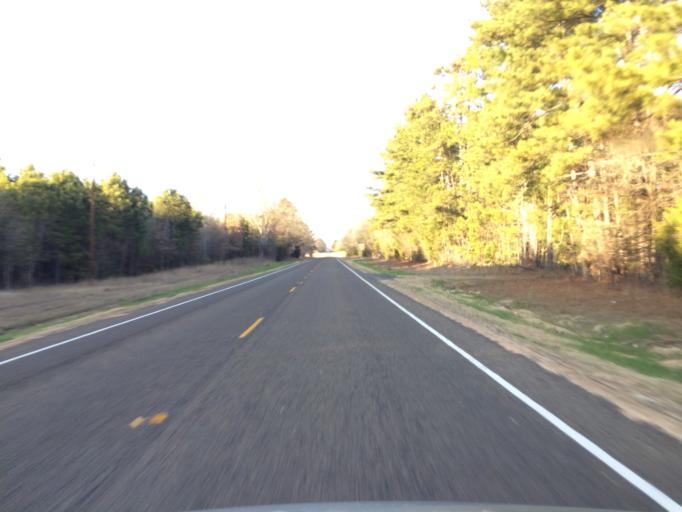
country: US
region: Texas
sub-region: Wood County
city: Hawkins
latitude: 32.6108
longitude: -95.2741
